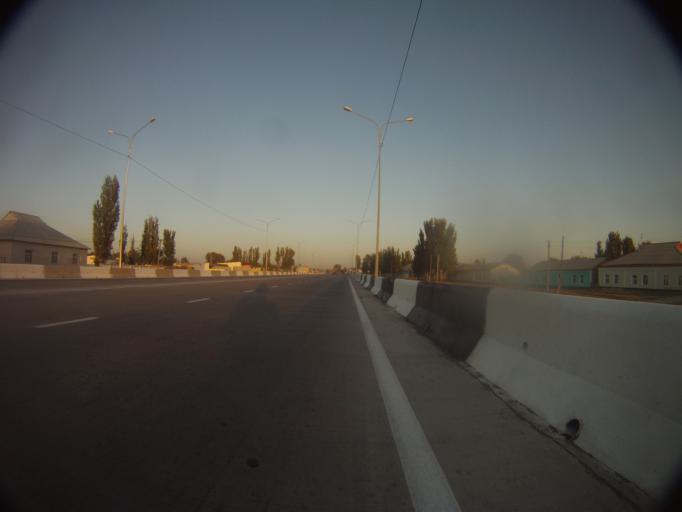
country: KZ
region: Ongtustik Qazaqstan
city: Turkestan
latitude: 43.2610
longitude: 68.3749
